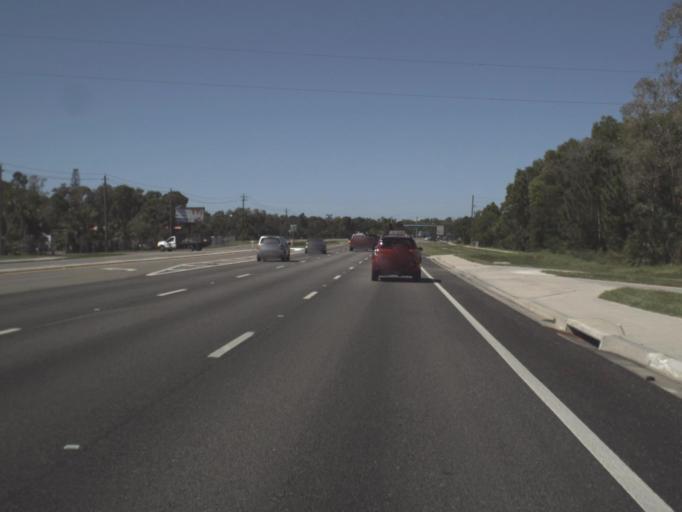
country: US
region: Florida
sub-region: Lee County
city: Estero
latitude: 26.4454
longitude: -81.8136
